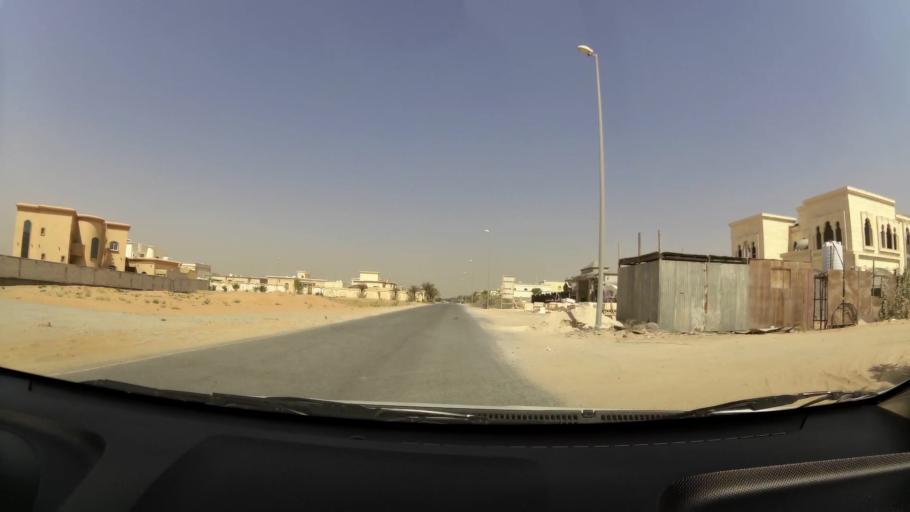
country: AE
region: Ajman
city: Ajman
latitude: 25.3953
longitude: 55.5485
